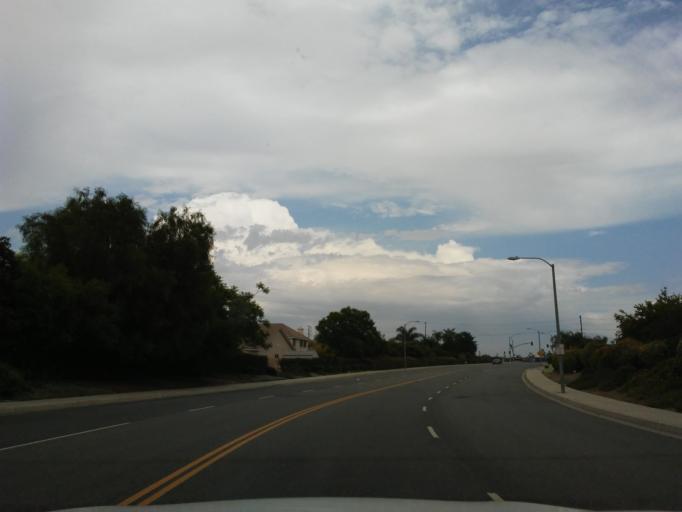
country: US
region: California
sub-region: San Bernardino County
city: Loma Linda
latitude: 34.0540
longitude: -117.2814
